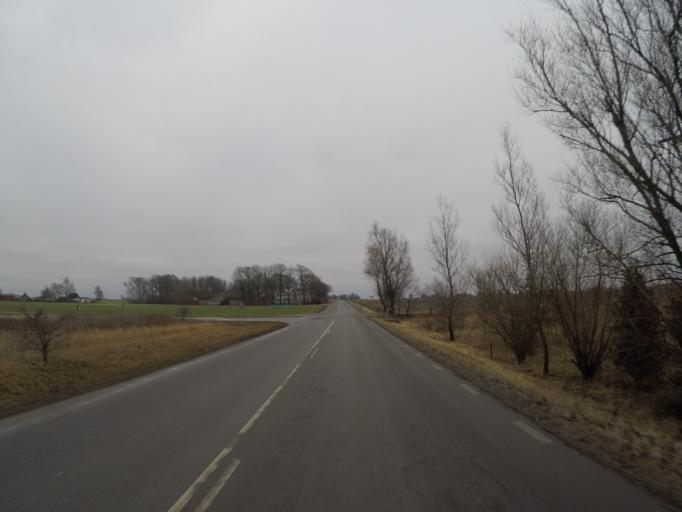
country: SE
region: Skane
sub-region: Hoors Kommun
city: Loberod
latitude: 55.7841
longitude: 13.4174
